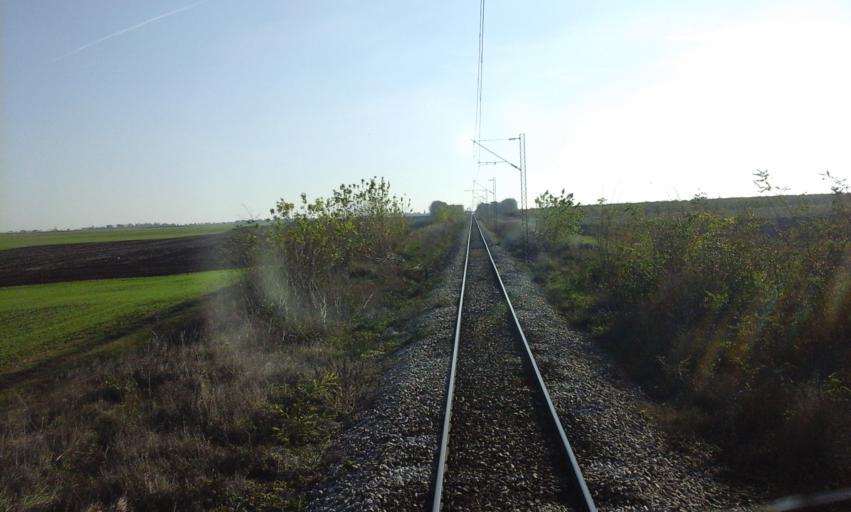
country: RS
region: Autonomna Pokrajina Vojvodina
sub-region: Severnobacki Okrug
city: Backa Topola
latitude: 45.7682
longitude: 19.6482
